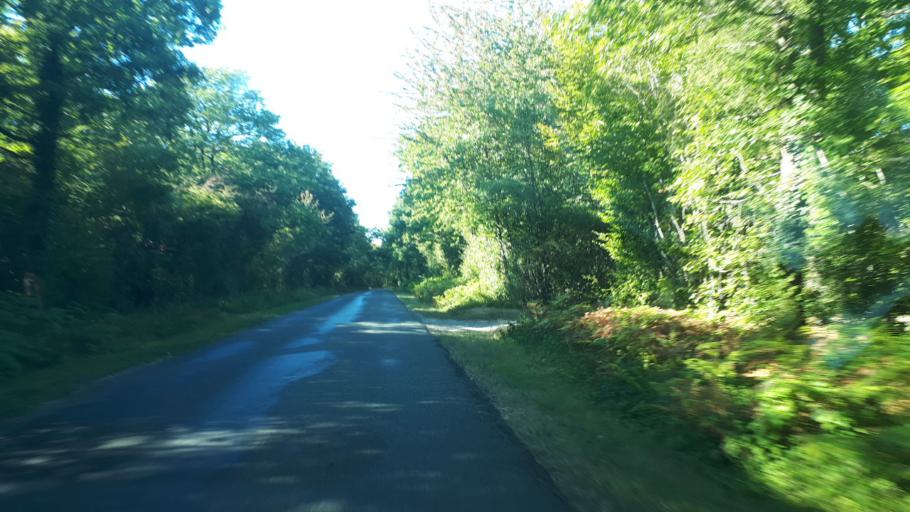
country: FR
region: Centre
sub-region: Departement du Cher
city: Sancerre
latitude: 47.2704
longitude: 2.7536
